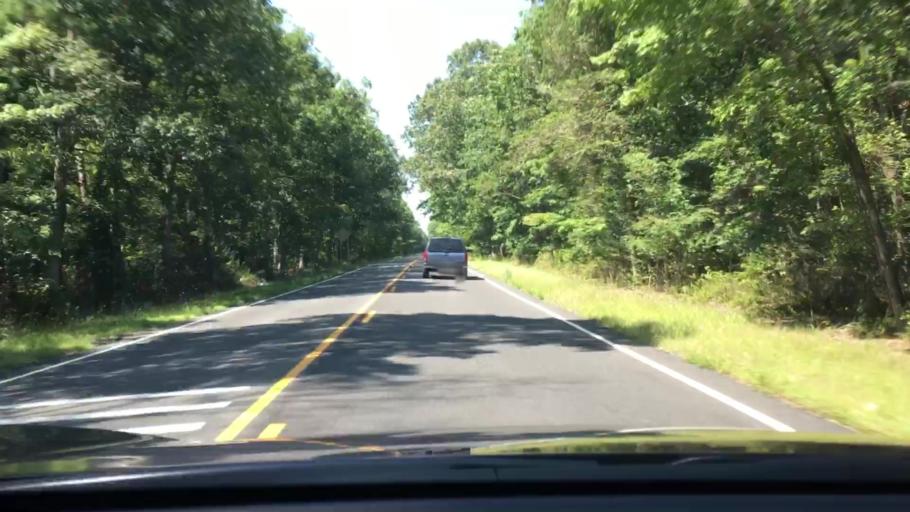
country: US
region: New Jersey
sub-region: Cape May County
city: Woodbine
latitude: 39.2614
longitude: -74.9161
